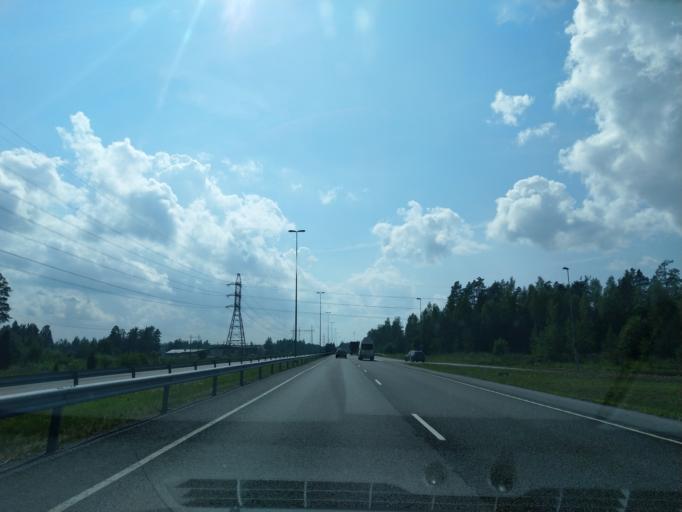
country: FI
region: South Karelia
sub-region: Lappeenranta
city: Joutseno
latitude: 61.1180
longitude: 28.4872
